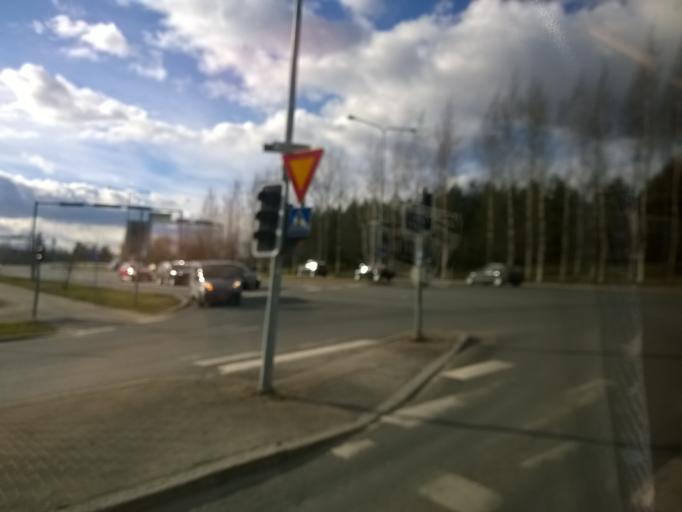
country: FI
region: Pirkanmaa
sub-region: Tampere
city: Tampere
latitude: 61.4776
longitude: 23.8743
